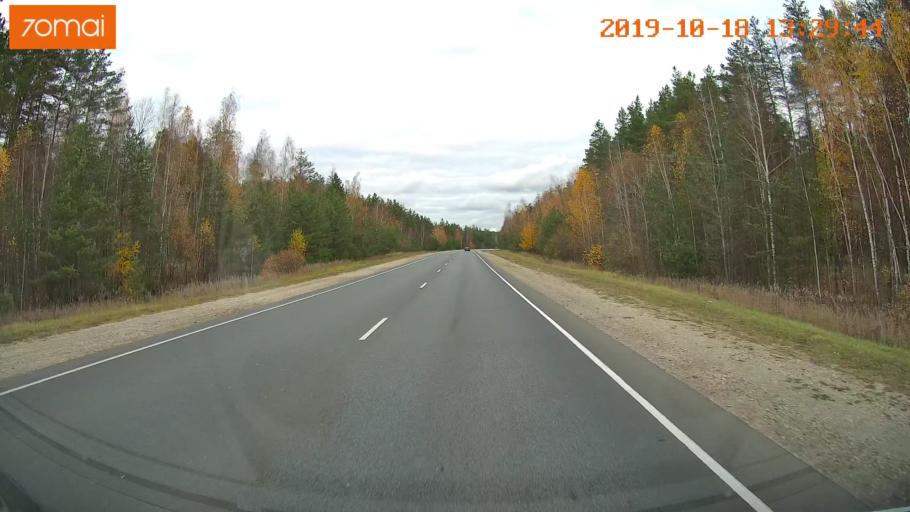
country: RU
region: Rjazan
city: Solotcha
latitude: 54.7994
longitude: 39.8769
